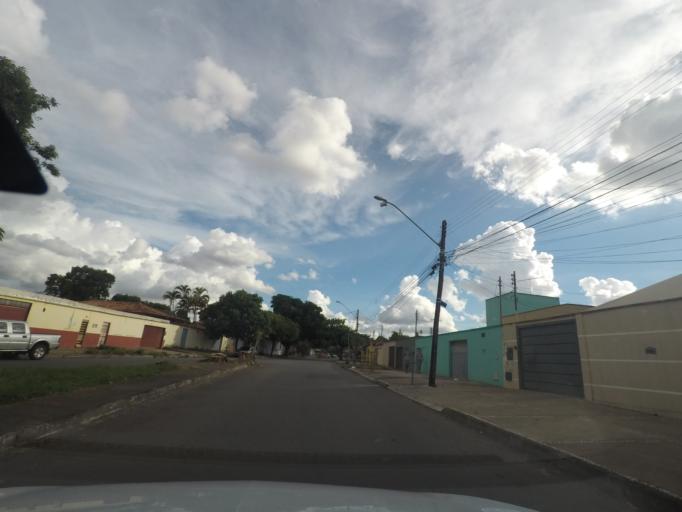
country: BR
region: Goias
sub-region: Goiania
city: Goiania
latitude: -16.7136
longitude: -49.3039
